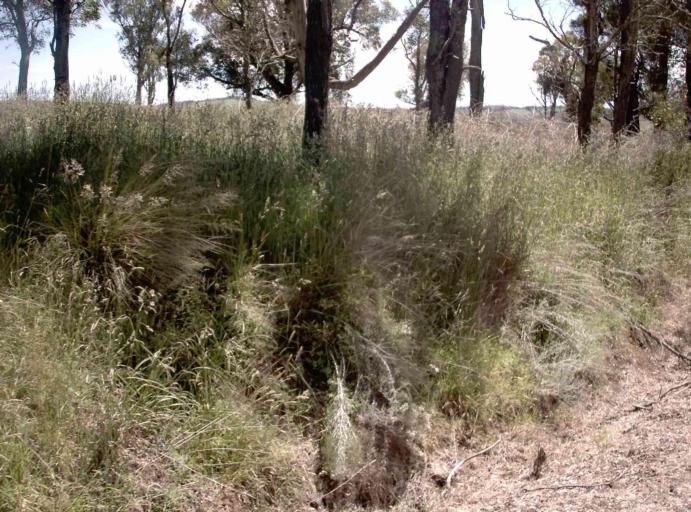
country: AU
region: Victoria
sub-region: East Gippsland
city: Lakes Entrance
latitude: -37.2492
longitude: 148.2525
